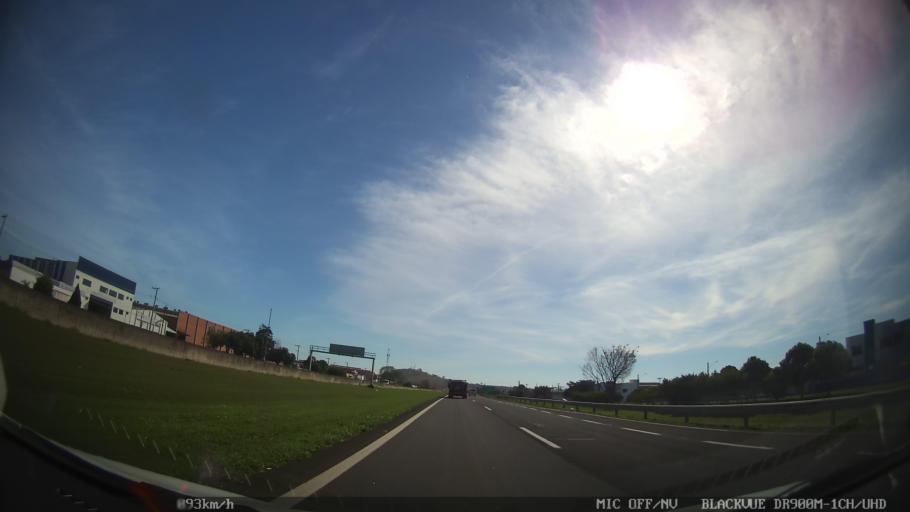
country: BR
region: Sao Paulo
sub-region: Leme
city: Leme
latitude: -22.1800
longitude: -47.3986
